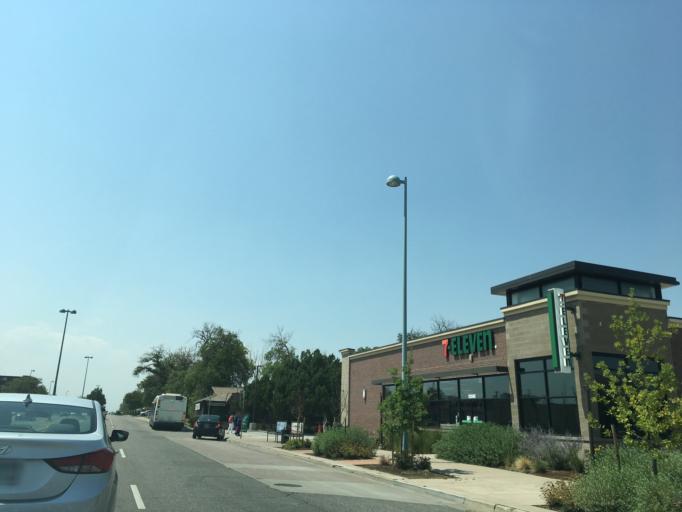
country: US
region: Colorado
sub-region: Adams County
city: Aurora
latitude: 39.7402
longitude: -104.8472
